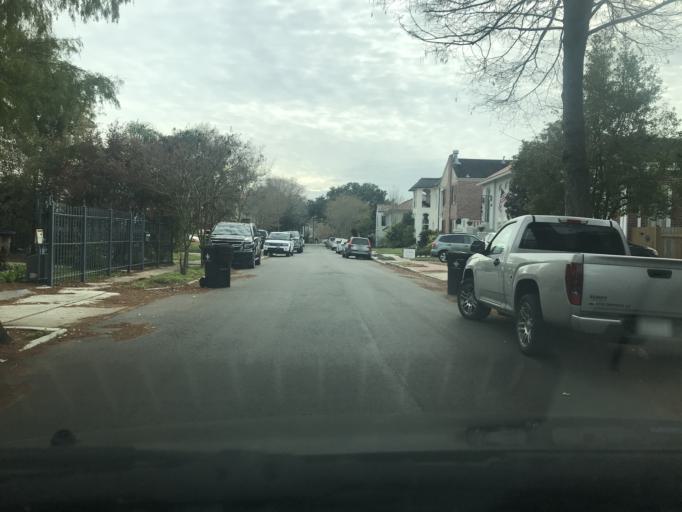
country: US
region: Louisiana
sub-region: Orleans Parish
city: New Orleans
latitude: 29.9524
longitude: -90.1093
